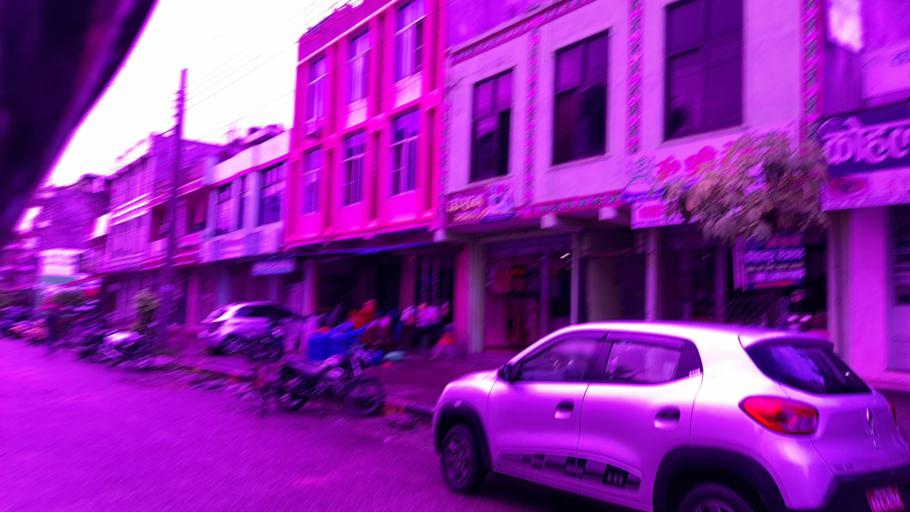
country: NP
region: Mid Western
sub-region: Bheri Zone
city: Nepalgunj
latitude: 28.1952
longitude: 81.6880
